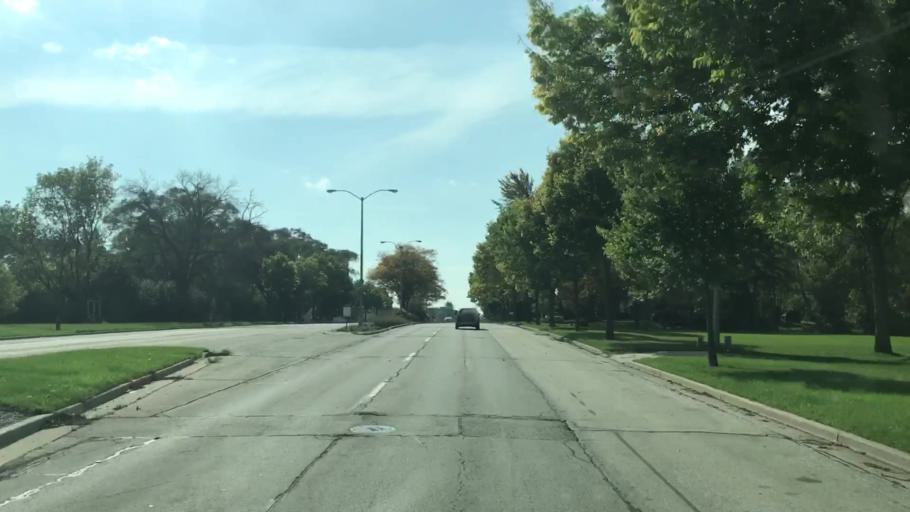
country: US
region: Wisconsin
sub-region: Waukesha County
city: Butler
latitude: 43.1655
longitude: -88.0445
